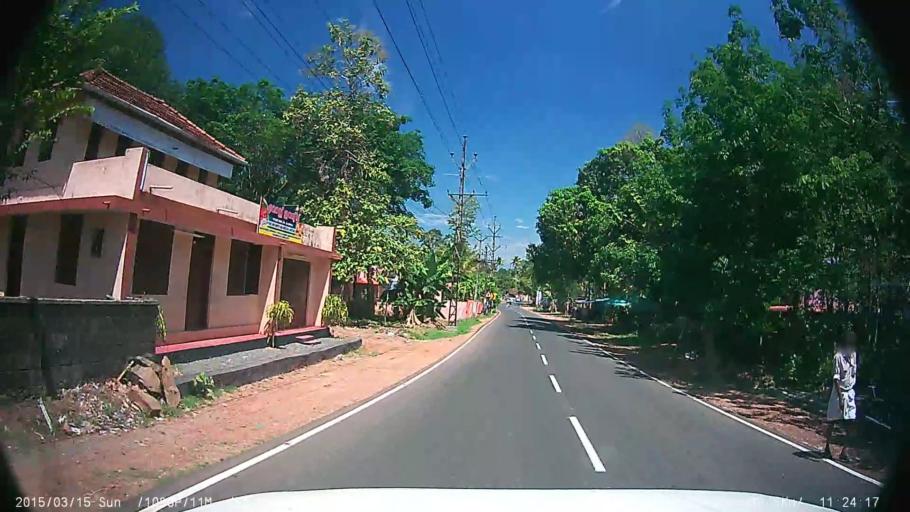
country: IN
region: Kerala
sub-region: Kottayam
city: Changanacheri
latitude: 9.4853
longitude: 76.5724
